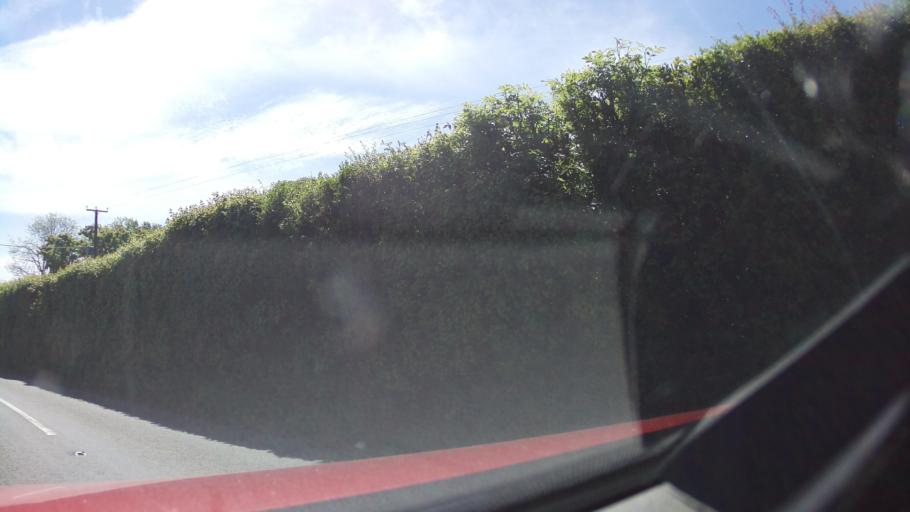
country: GB
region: England
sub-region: Devon
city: Honiton
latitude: 50.8133
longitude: -3.2443
